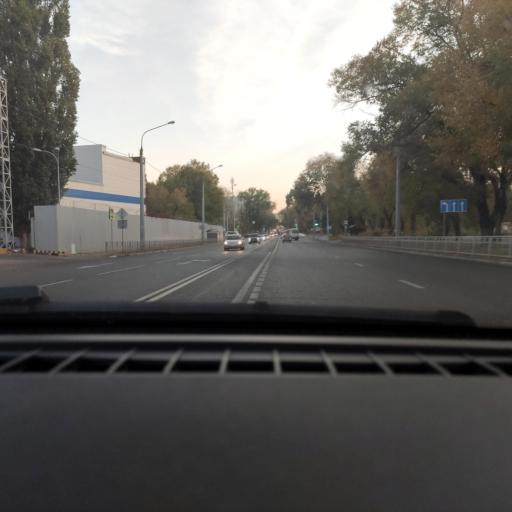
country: RU
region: Voronezj
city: Maslovka
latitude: 51.6022
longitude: 39.2438
